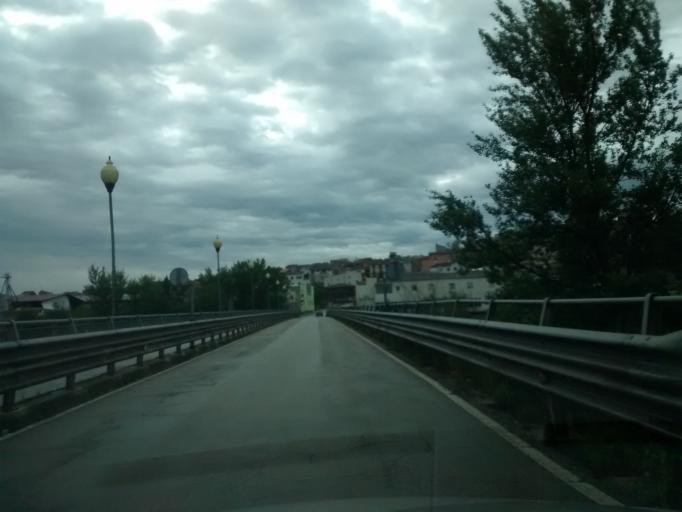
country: ES
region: Aragon
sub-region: Provincia de Zaragoza
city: Maella
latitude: 41.1193
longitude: 0.1426
